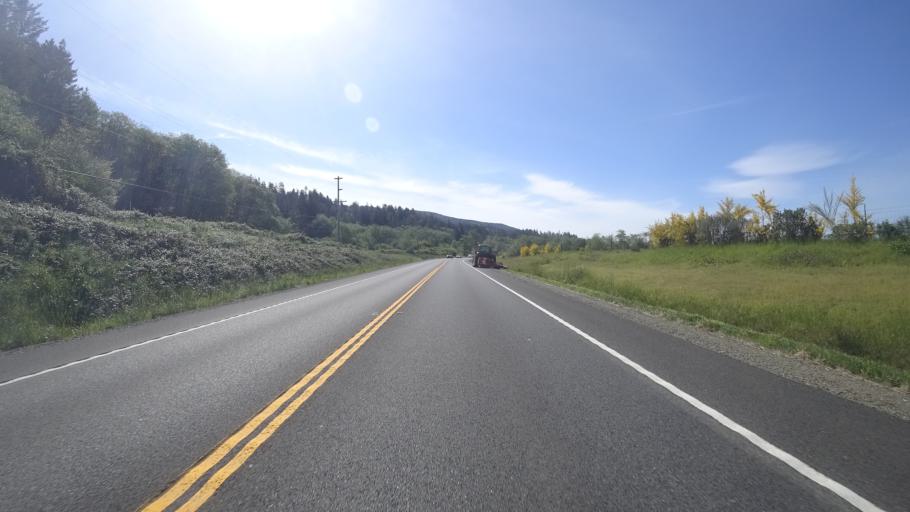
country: US
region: California
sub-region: Del Norte County
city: Bertsch-Oceanview
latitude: 41.9228
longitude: -124.1383
